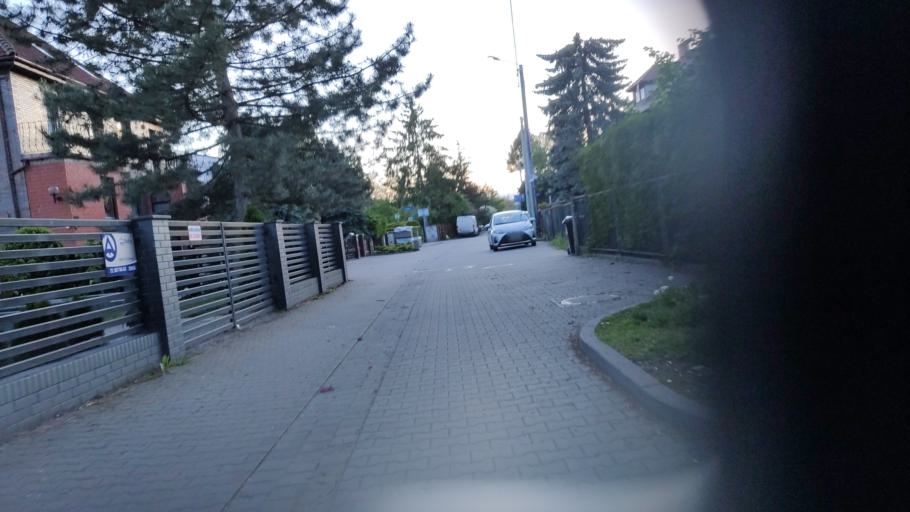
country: PL
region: Lower Silesian Voivodeship
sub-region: Powiat wroclawski
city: Wroclaw
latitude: 51.0744
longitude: 17.0382
